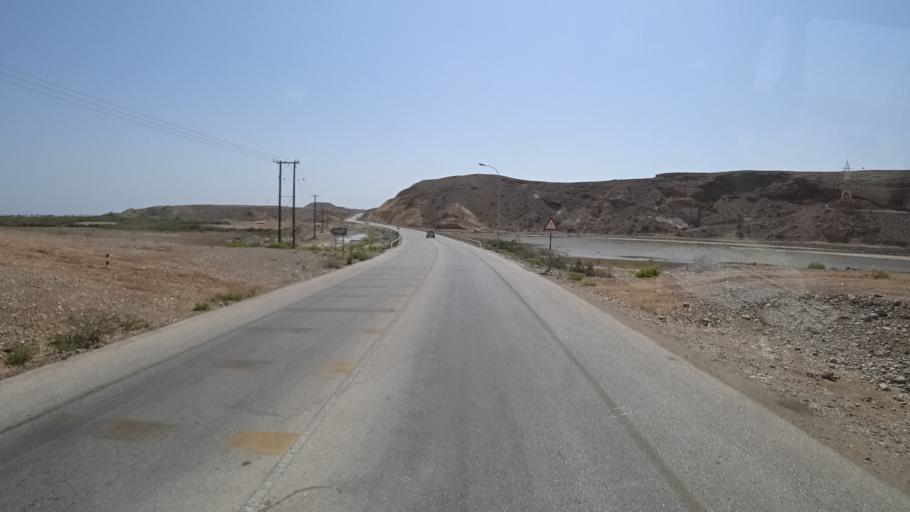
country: OM
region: Ash Sharqiyah
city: Sur
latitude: 22.5421
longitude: 59.5080
